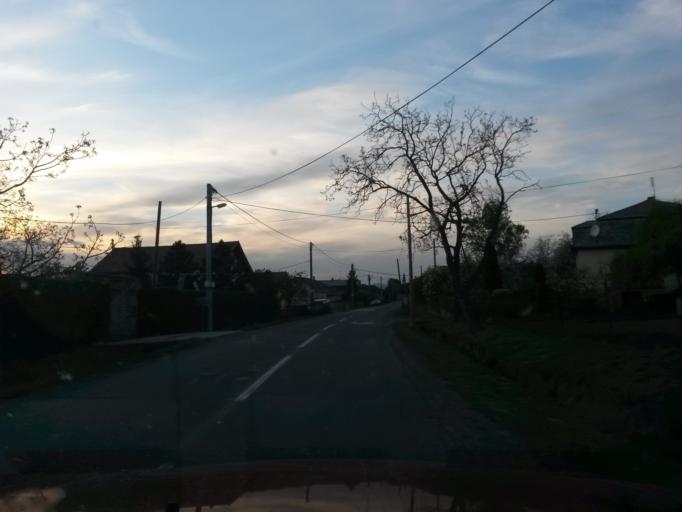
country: HU
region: Borsod-Abauj-Zemplen
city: Satoraljaujhely
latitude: 48.4851
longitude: 21.6413
